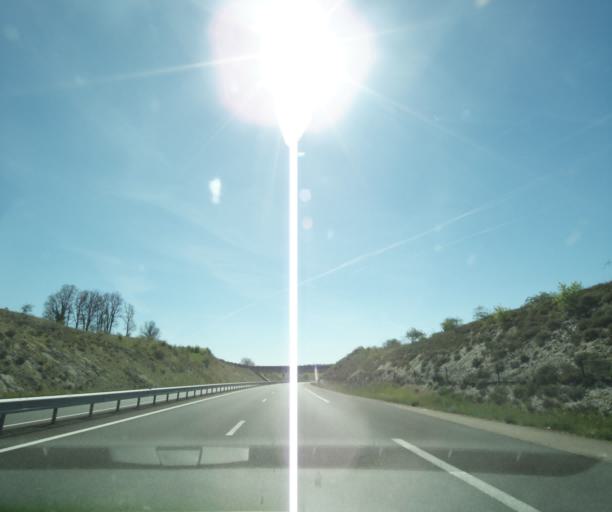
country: FR
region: Midi-Pyrenees
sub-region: Departement du Lot
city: Le Vigan
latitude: 44.6302
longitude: 1.5201
